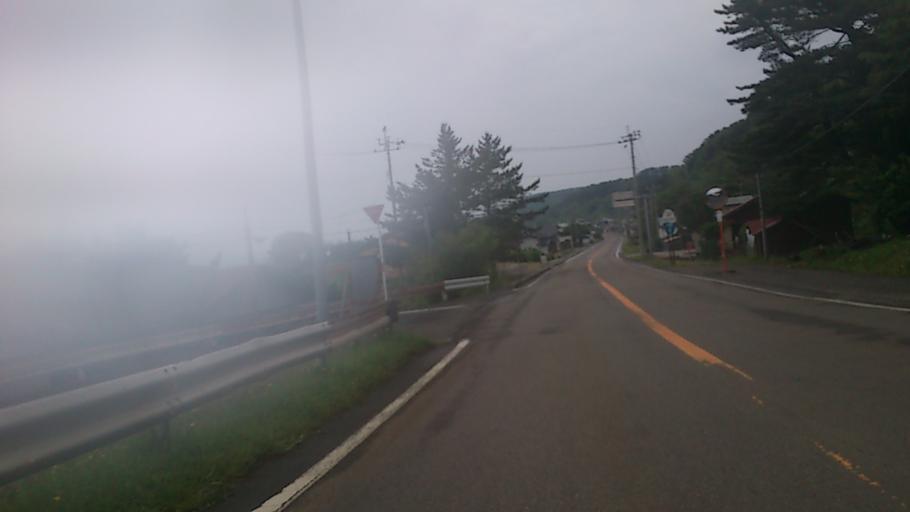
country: JP
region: Akita
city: Noshiromachi
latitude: 40.4890
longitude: 139.9497
